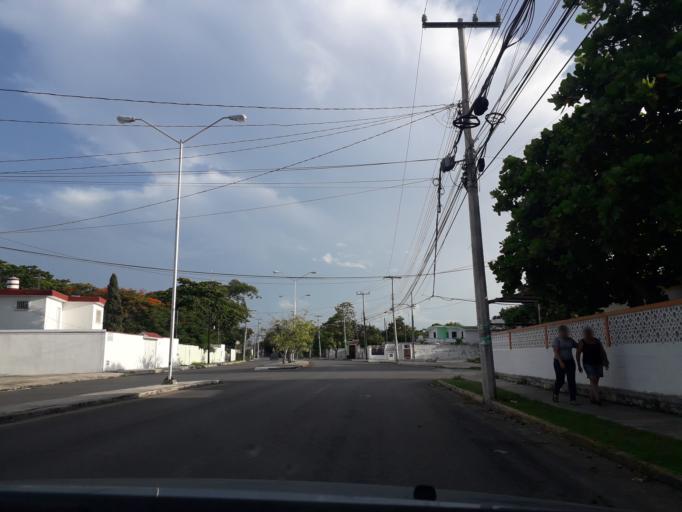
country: MX
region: Yucatan
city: Merida
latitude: 21.0215
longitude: -89.6313
